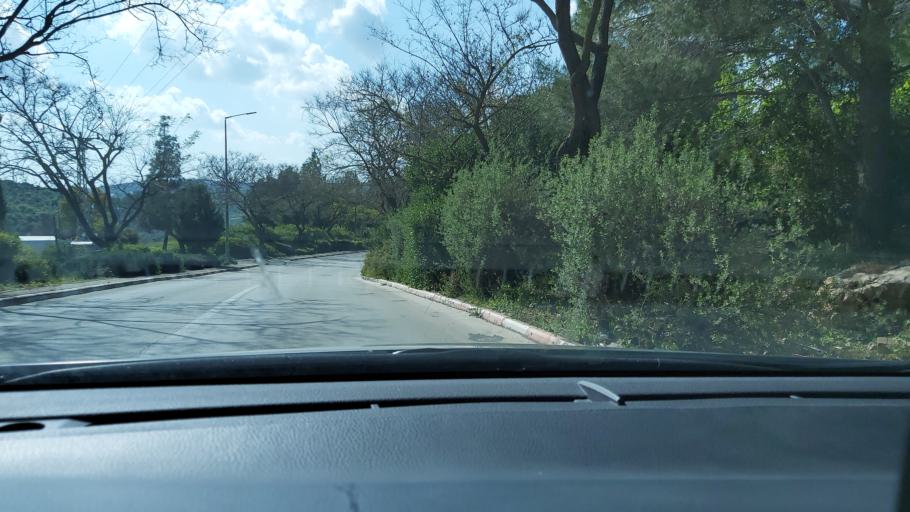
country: IL
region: Jerusalem
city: Ariel
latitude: 32.1013
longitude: 35.1670
